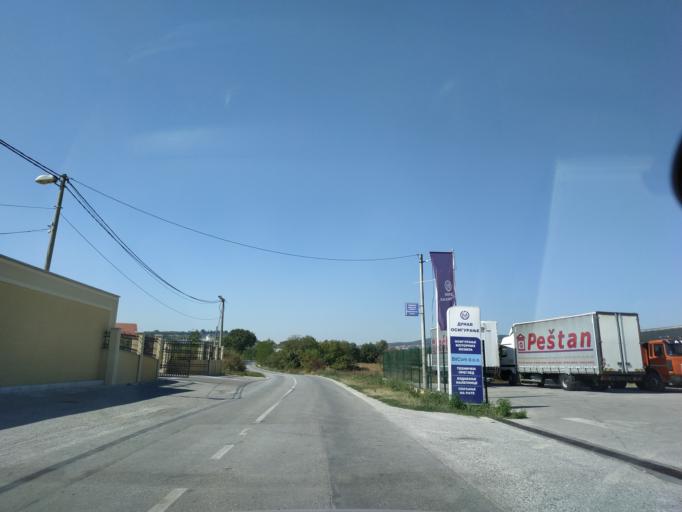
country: RS
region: Central Serbia
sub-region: Sumadijski Okrug
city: Arangelovac
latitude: 44.2932
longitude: 20.6018
